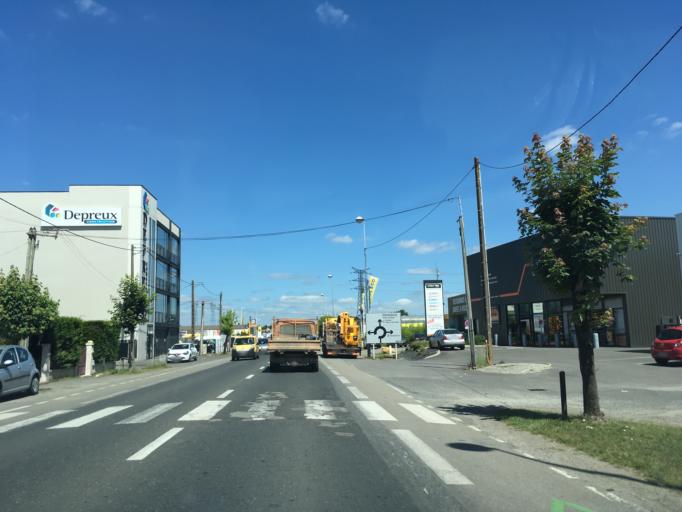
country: FR
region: Pays de la Loire
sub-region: Departement de la Loire-Atlantique
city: Les Sorinieres
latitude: 47.1538
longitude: -1.5362
